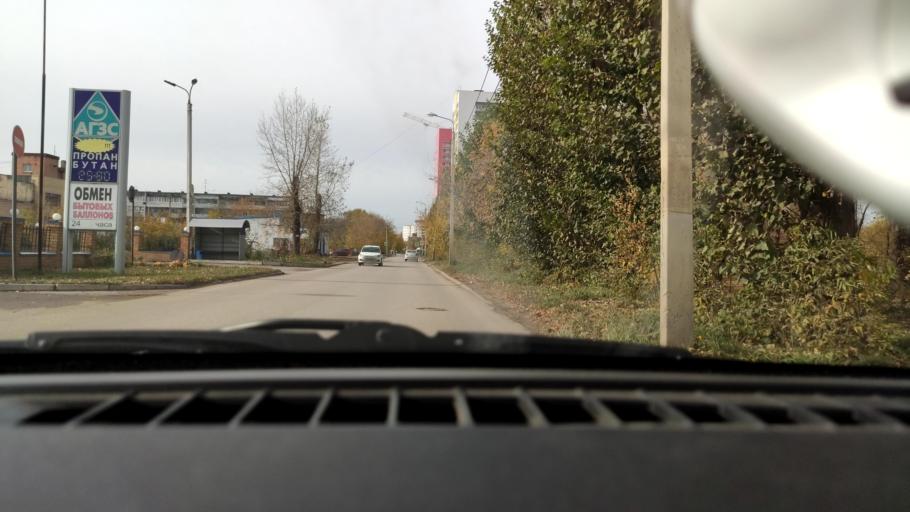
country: RU
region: Perm
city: Perm
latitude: 57.9684
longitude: 56.2397
